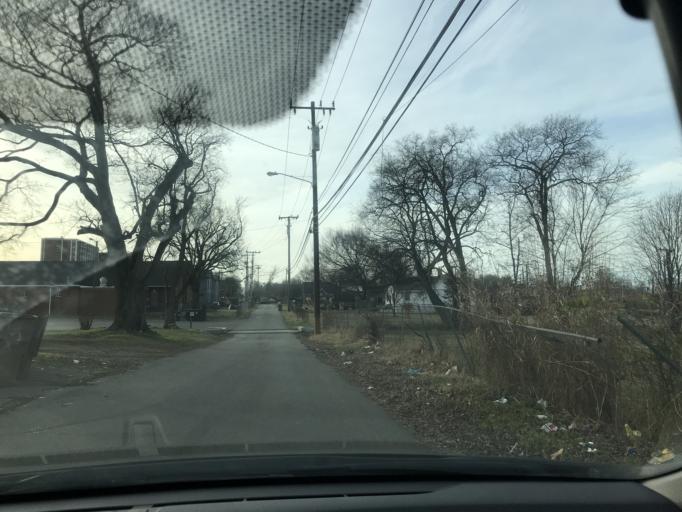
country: US
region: Tennessee
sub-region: Davidson County
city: Nashville
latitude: 36.1686
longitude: -86.8187
